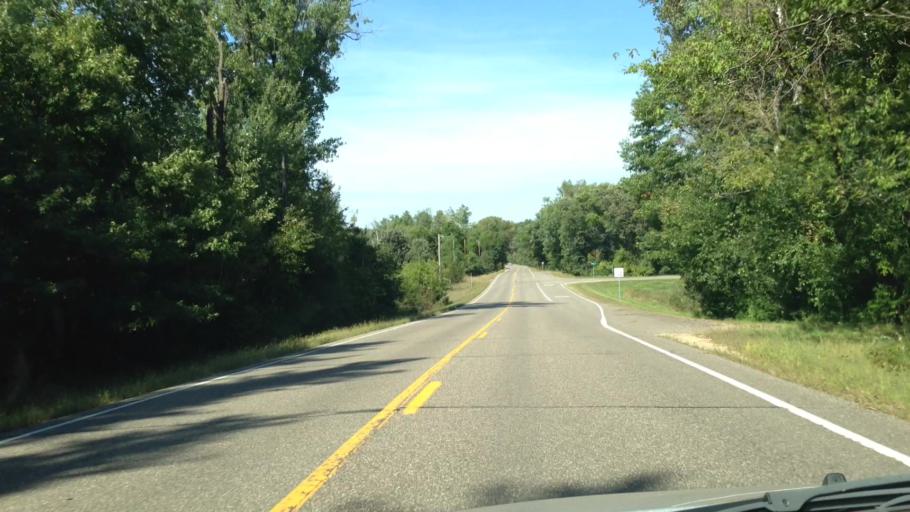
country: US
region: Minnesota
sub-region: Washington County
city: Stillwater
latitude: 45.1117
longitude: -92.8127
